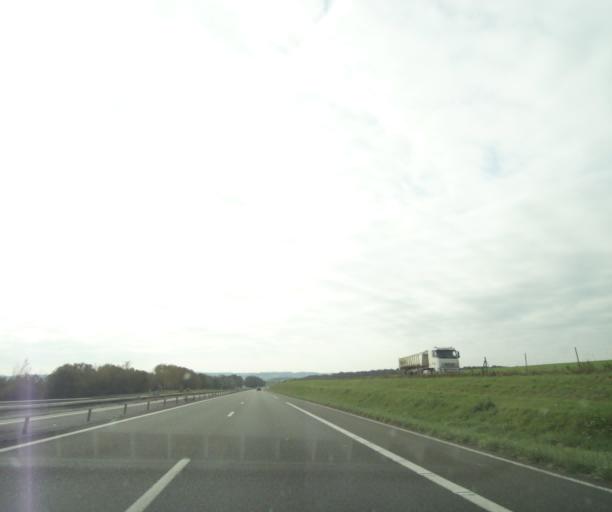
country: FR
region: Ile-de-France
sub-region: Departement de Seine-et-Marne
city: Sammeron
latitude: 48.9779
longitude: 3.0726
